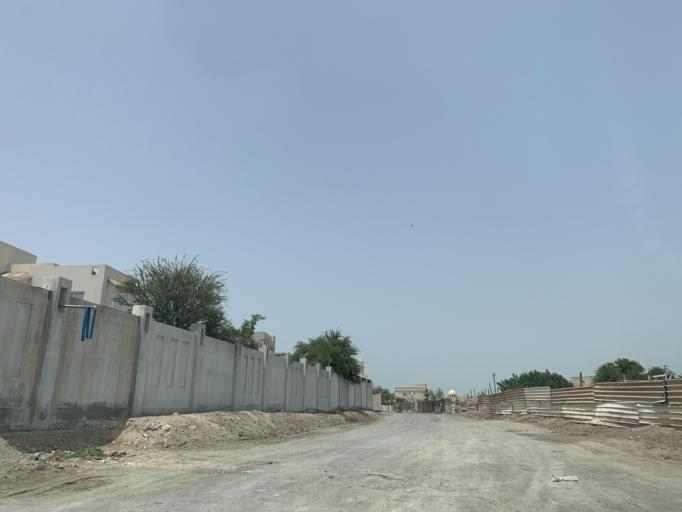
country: BH
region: Northern
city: Sitrah
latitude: 26.1534
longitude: 50.5871
